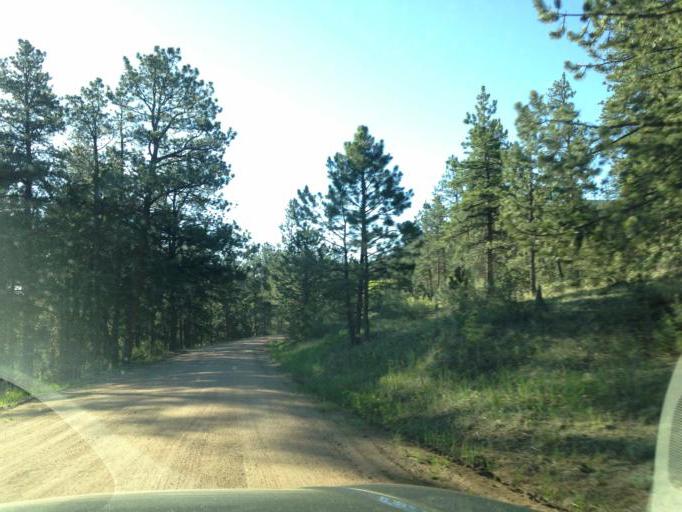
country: US
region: Colorado
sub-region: Jefferson County
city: Evergreen
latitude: 39.4070
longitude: -105.5073
